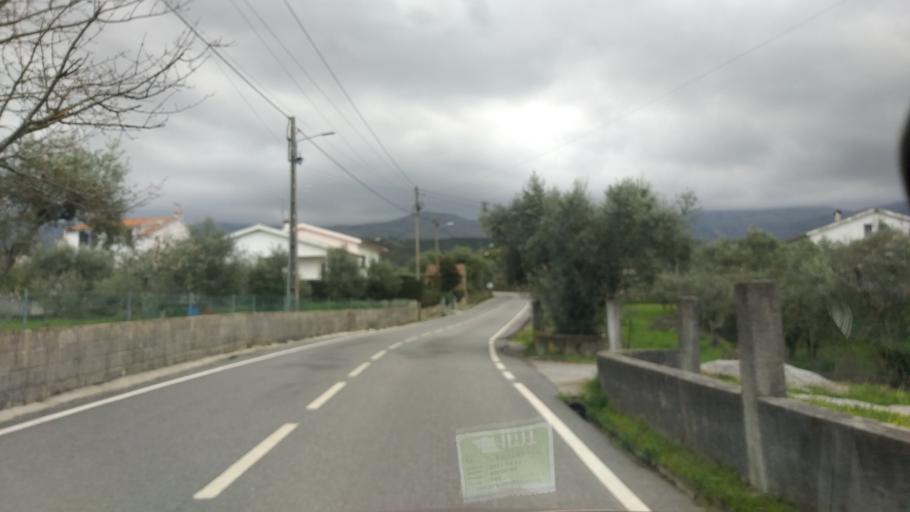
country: PT
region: Guarda
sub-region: Seia
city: Seia
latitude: 40.4740
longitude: -7.6376
